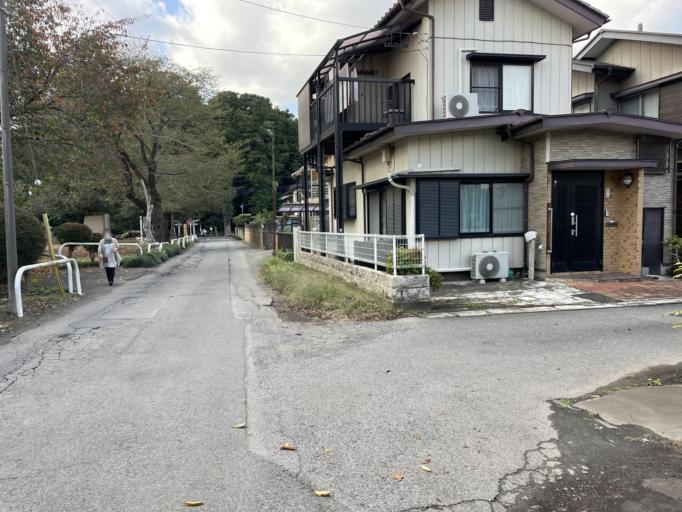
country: JP
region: Tochigi
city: Oyama
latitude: 36.2815
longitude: 139.7762
